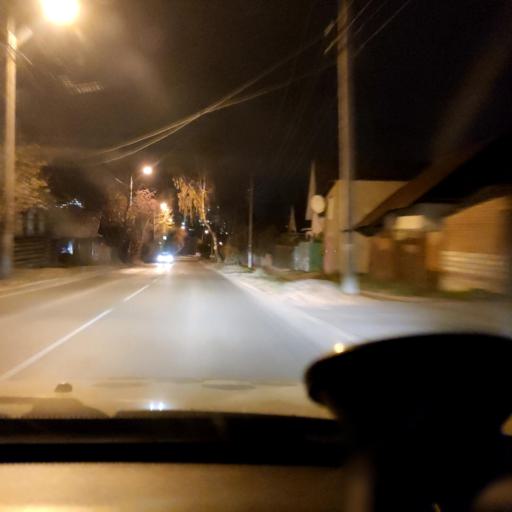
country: RU
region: Perm
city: Perm
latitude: 58.0222
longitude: 56.3127
